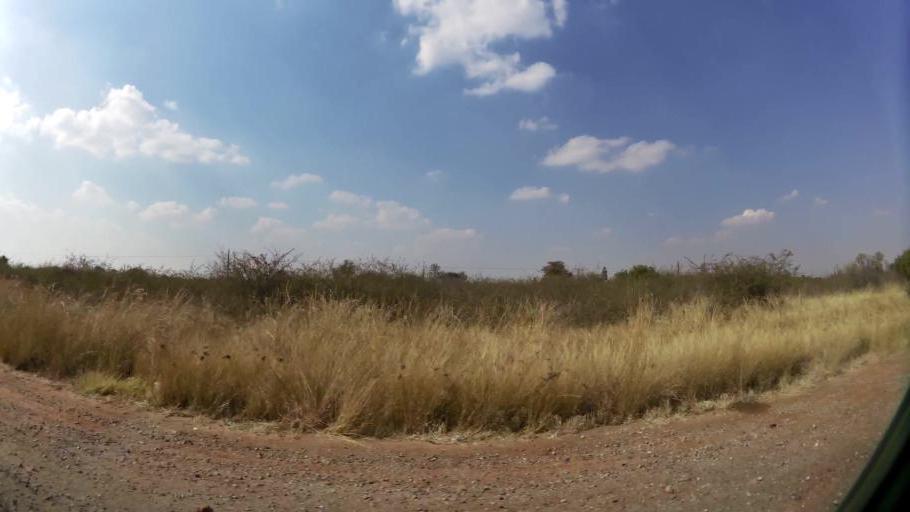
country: ZA
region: North-West
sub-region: Bojanala Platinum District Municipality
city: Rustenburg
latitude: -25.5146
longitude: 27.1007
